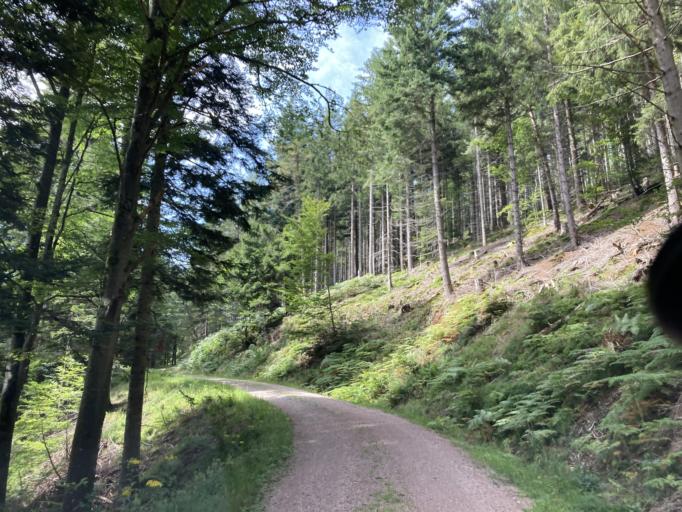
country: DE
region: Baden-Wuerttemberg
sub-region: Freiburg Region
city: Schonach im Schwarzwald
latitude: 48.1632
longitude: 8.1477
